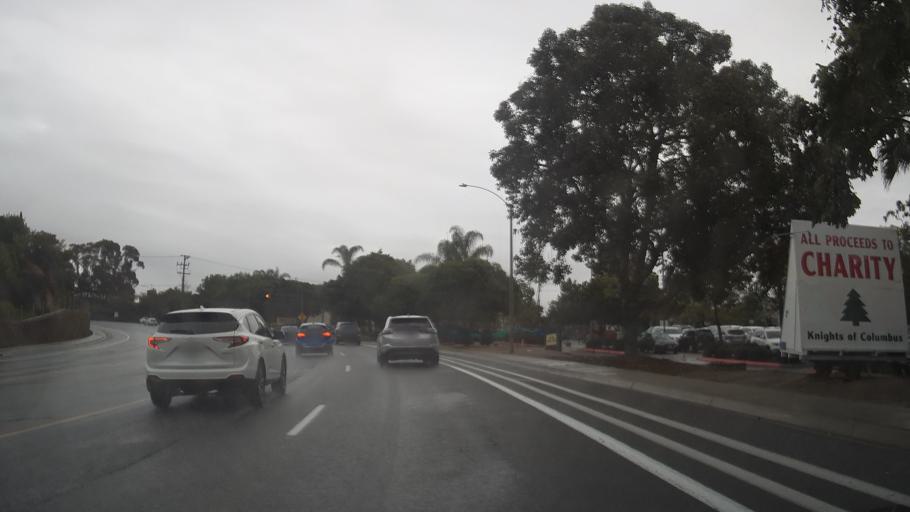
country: US
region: California
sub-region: San Diego County
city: Encinitas
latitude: 33.0456
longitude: -117.2714
